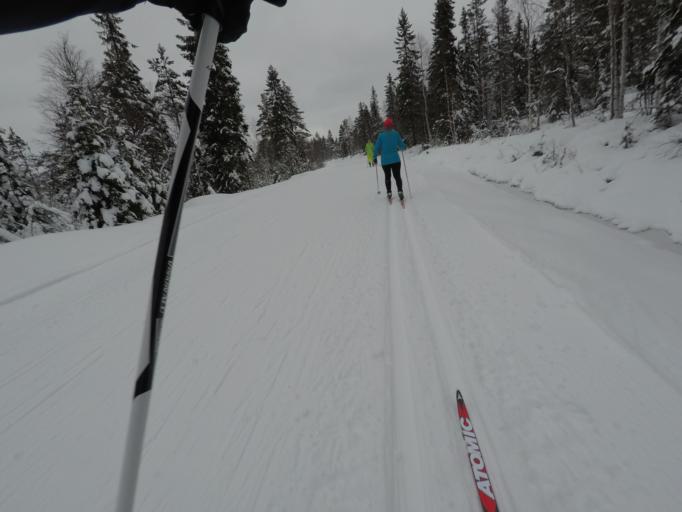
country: SE
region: Dalarna
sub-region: Ludvika Kommun
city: Abborrberget
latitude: 60.1394
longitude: 14.4854
